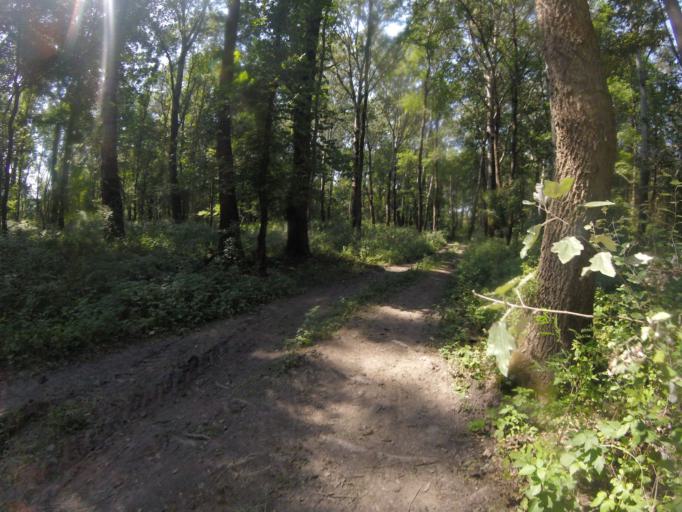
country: HU
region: Tolna
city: Bata
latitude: 46.2006
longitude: 18.8493
